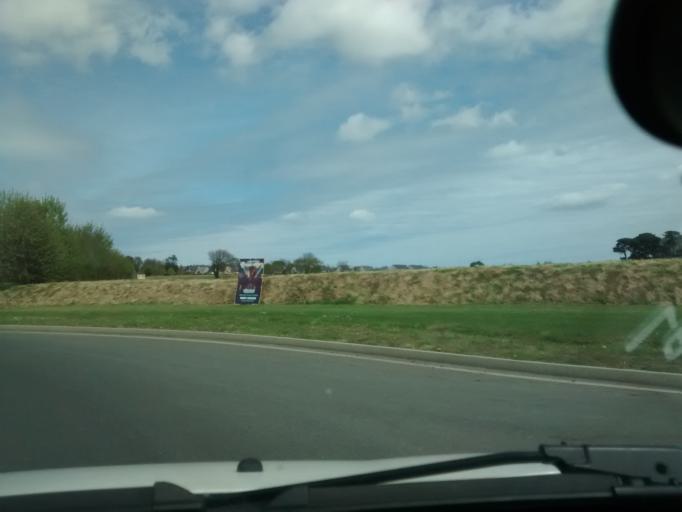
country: FR
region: Brittany
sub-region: Departement des Cotes-d'Armor
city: Minihy-Treguier
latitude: 48.7727
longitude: -3.2377
